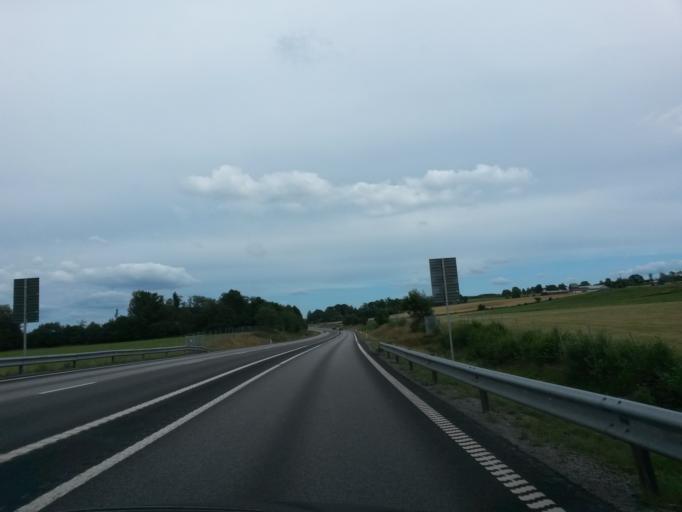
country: SE
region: Vaestra Goetaland
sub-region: Marks Kommun
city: Kinna
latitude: 57.4775
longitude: 12.6216
